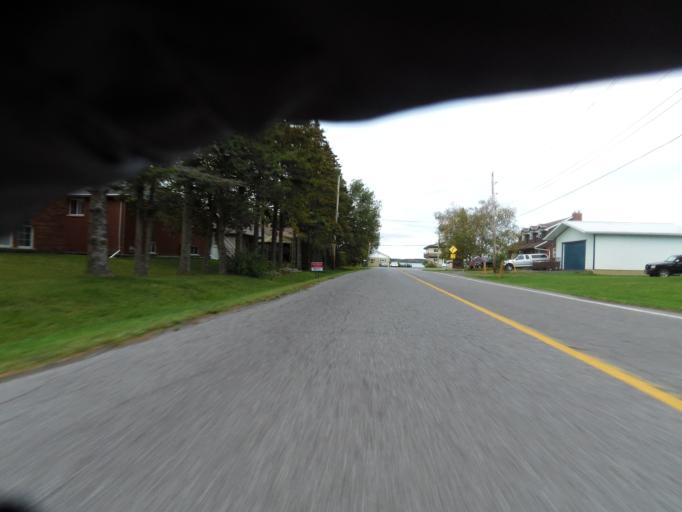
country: CA
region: Ontario
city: Quinte West
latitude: 44.0187
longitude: -77.7300
